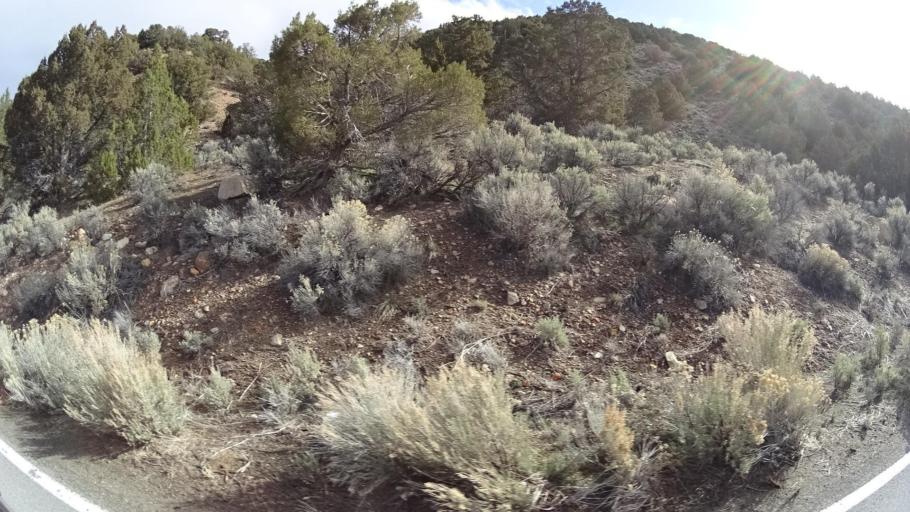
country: US
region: Nevada
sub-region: Washoe County
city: Cold Springs
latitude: 39.9056
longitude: -120.0006
